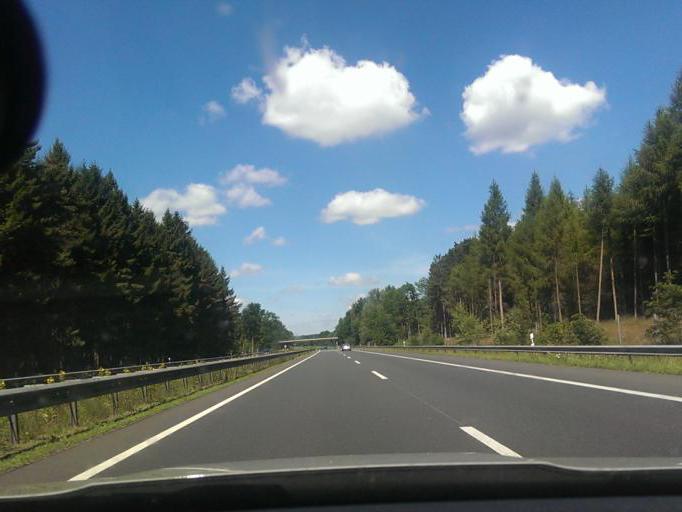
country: DE
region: Lower Saxony
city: Hauslingen
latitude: 52.8989
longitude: 9.4190
